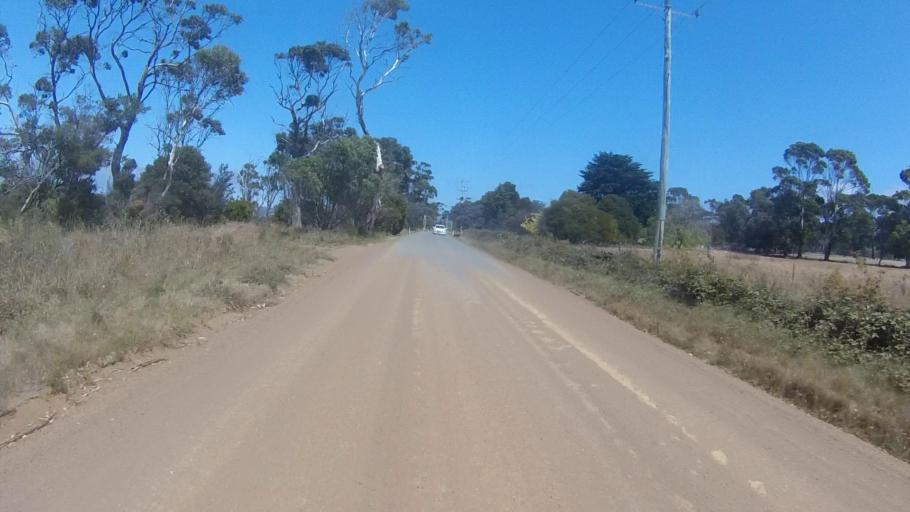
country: AU
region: Tasmania
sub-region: Sorell
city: Sorell
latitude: -42.8391
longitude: 147.8530
